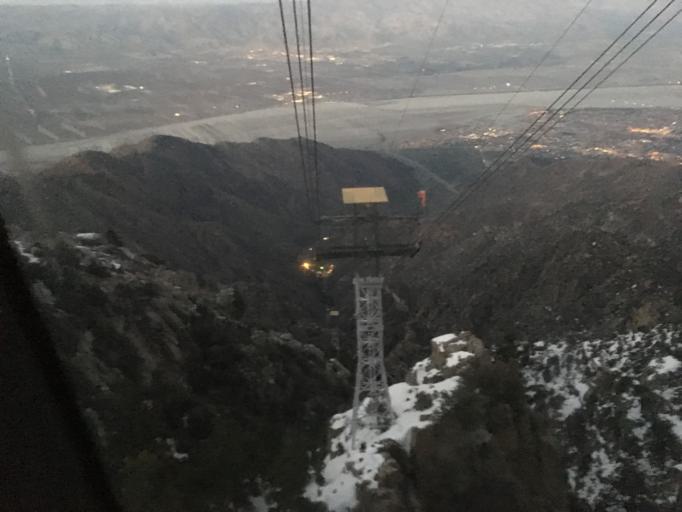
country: US
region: California
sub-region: Riverside County
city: Palm Springs
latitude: 33.8142
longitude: -116.6374
